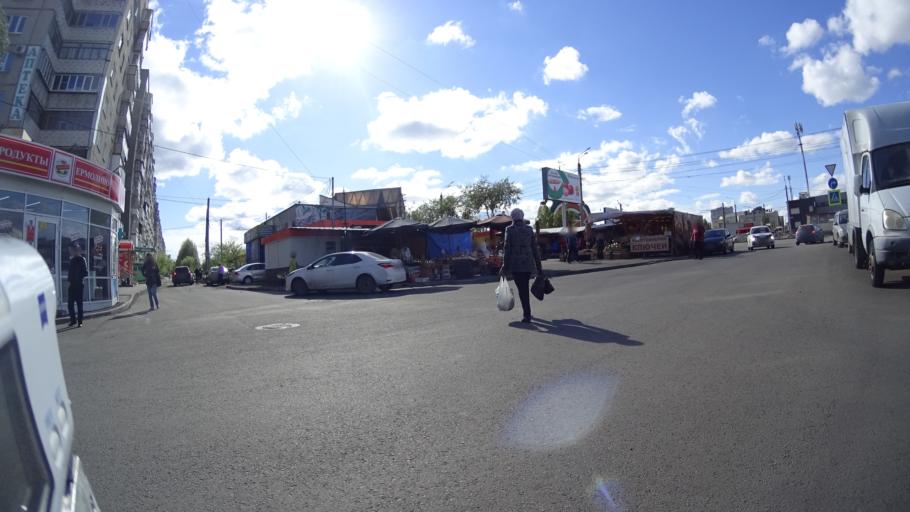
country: RU
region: Chelyabinsk
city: Roshchino
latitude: 55.1815
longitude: 61.2912
